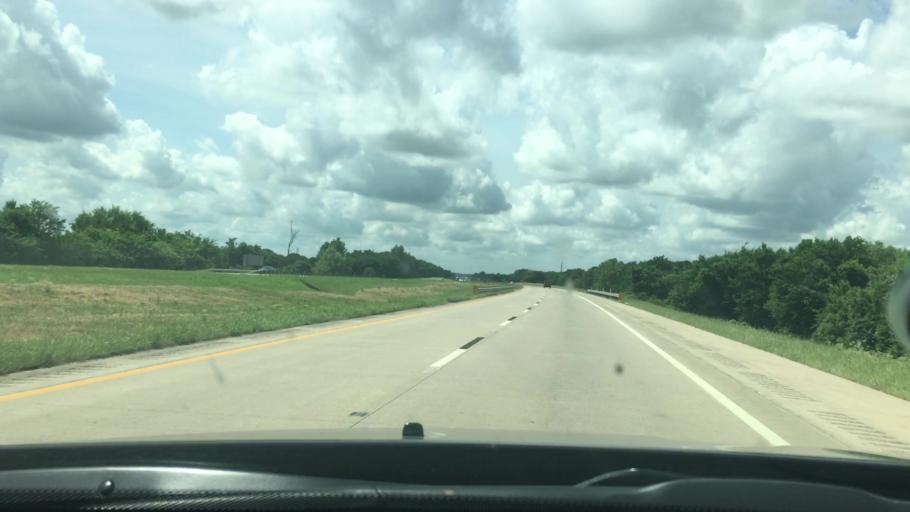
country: US
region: Oklahoma
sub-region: Love County
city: Marietta
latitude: 33.8090
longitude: -97.1347
